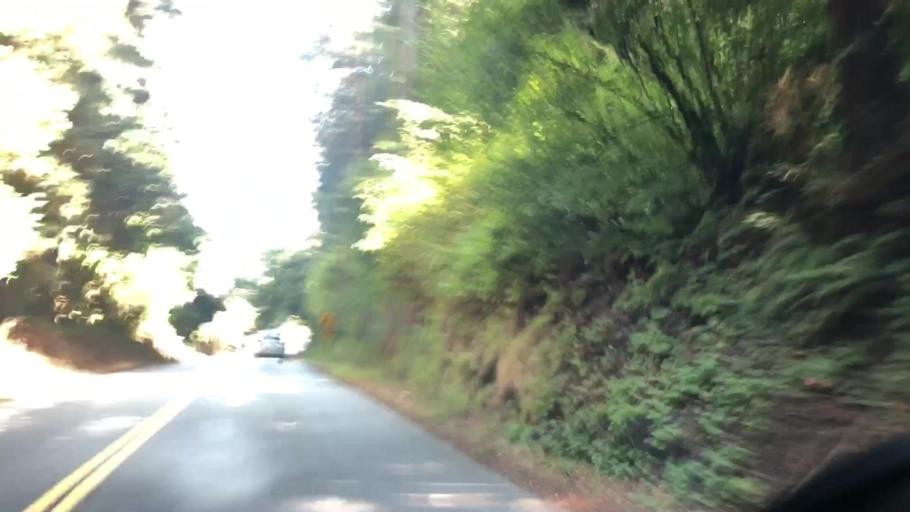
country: US
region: California
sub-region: Santa Cruz County
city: Corralitos
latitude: 37.0089
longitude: -121.8108
